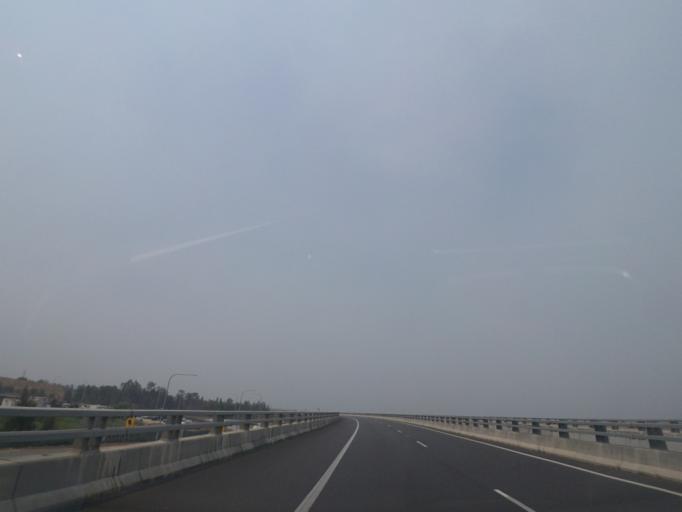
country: AU
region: New South Wales
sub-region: Ballina
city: Ballina
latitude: -28.8618
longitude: 153.5181
